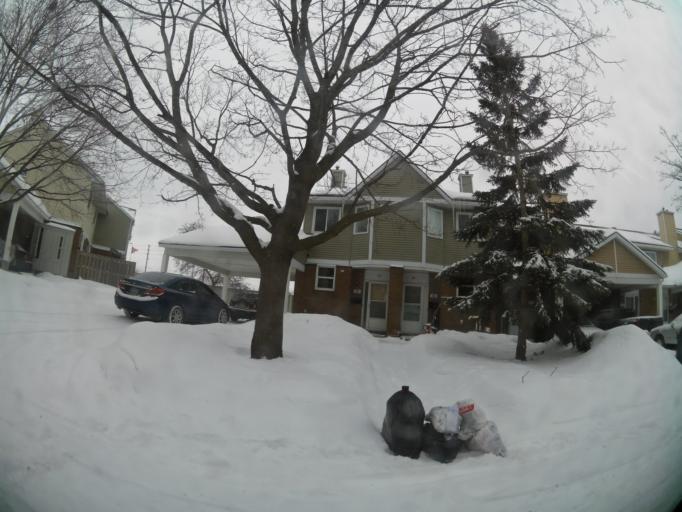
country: CA
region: Ontario
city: Ottawa
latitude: 45.3704
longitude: -75.6220
